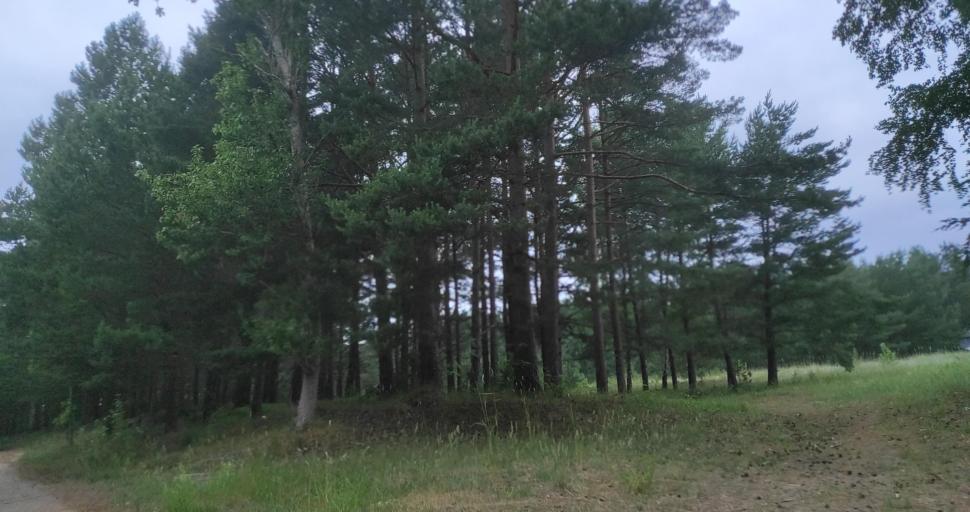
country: LV
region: Pavilostas
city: Pavilosta
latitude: 56.8883
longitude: 21.1930
